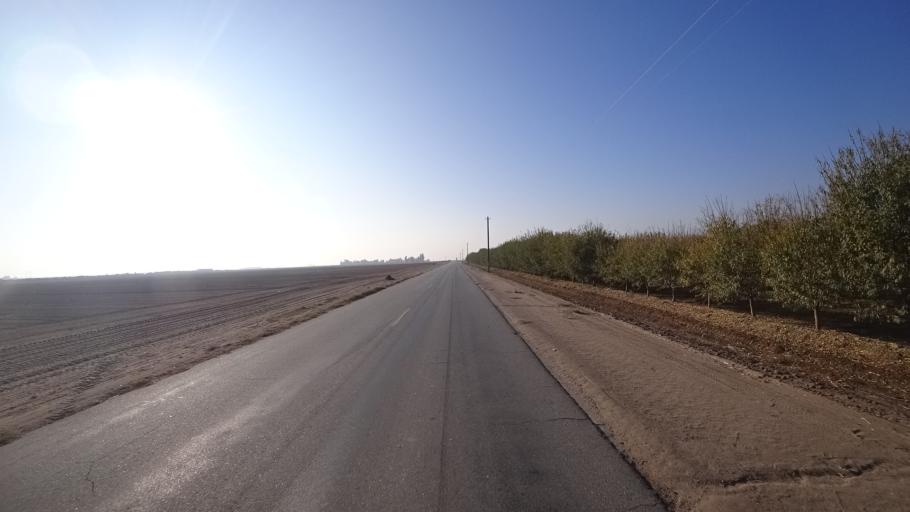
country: US
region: California
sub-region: Kern County
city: Greenfield
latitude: 35.2470
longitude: -118.9854
